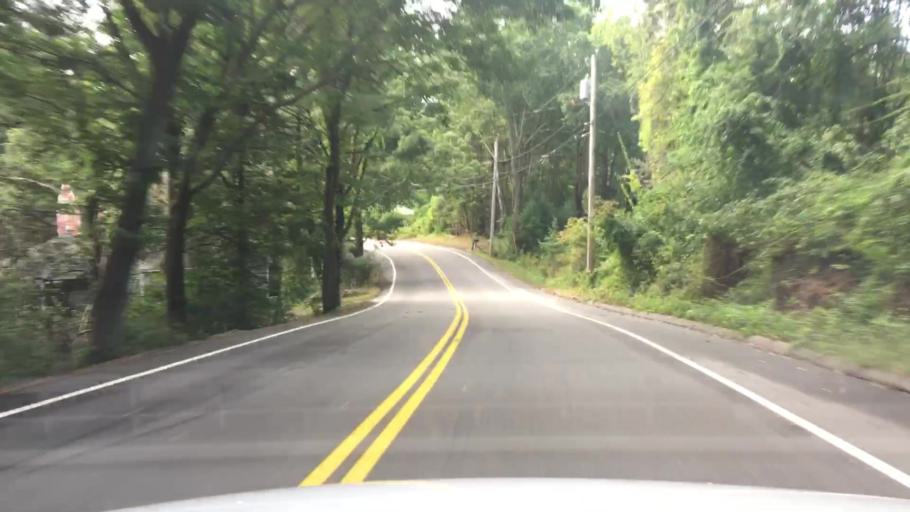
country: US
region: Maine
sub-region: York County
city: Kittery Point
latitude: 43.0860
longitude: -70.7114
